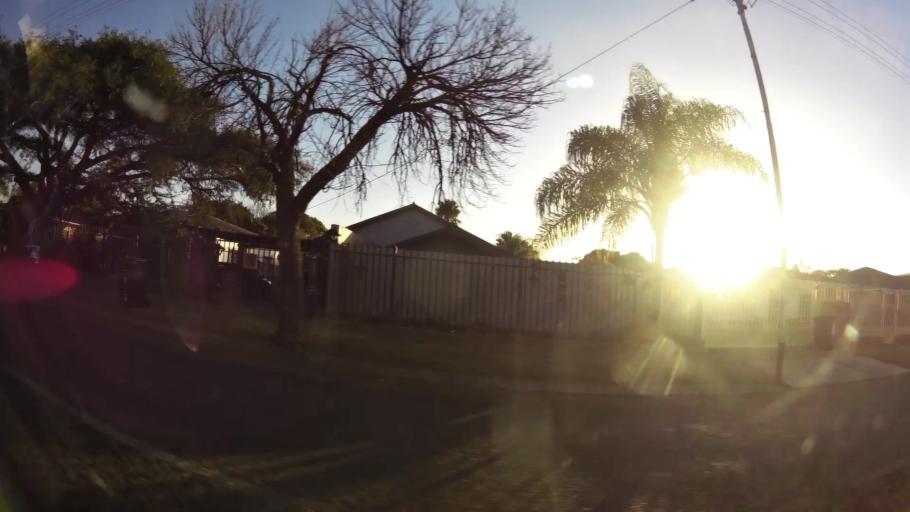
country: ZA
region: Gauteng
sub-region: City of Tshwane Metropolitan Municipality
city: Pretoria
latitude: -25.7060
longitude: 28.2361
